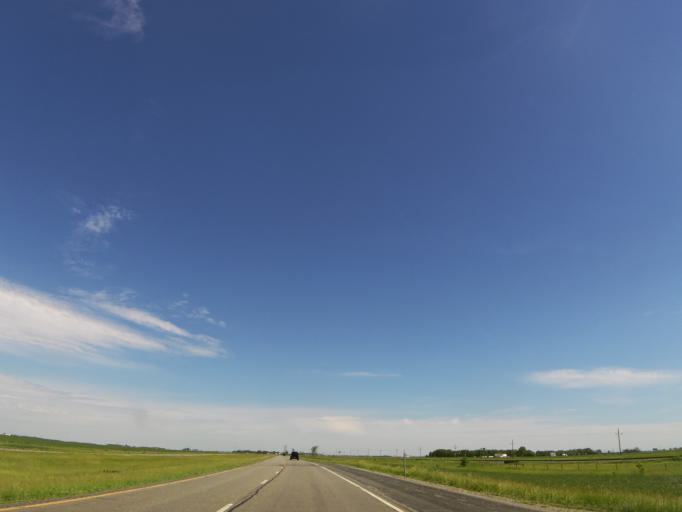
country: US
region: North Dakota
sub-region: Traill County
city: Hillsboro
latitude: 47.2024
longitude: -96.9903
